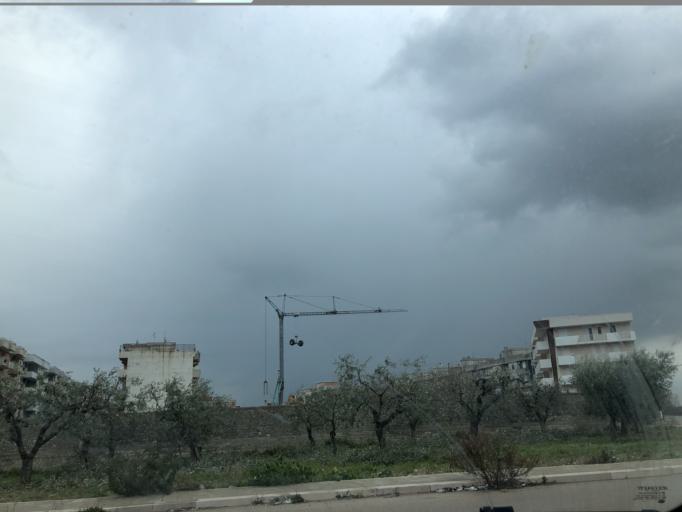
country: IT
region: Apulia
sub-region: Provincia di Foggia
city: Lucera
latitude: 41.5026
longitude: 15.3434
